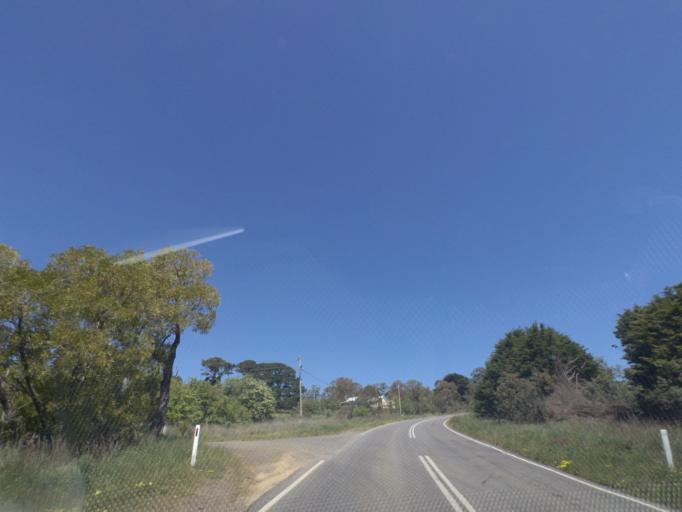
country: AU
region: Victoria
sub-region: Hume
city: Sunbury
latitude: -37.3022
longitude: 144.6868
